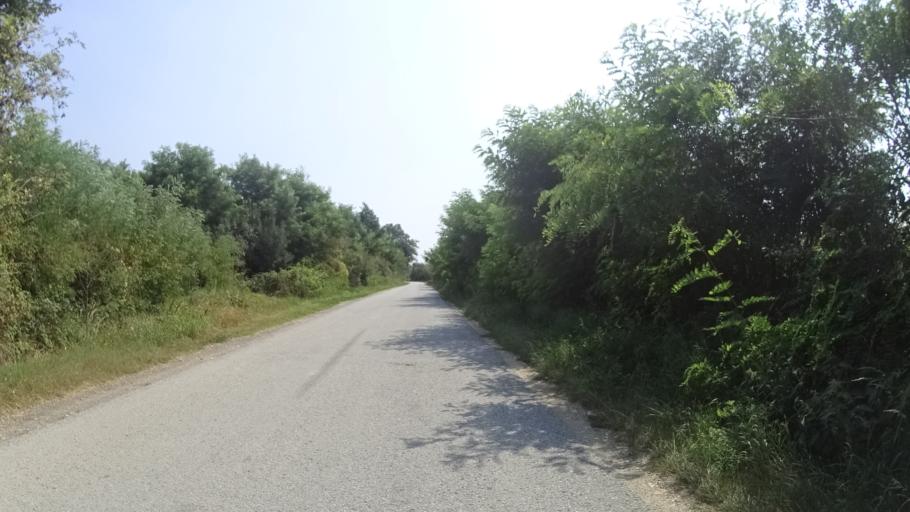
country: HR
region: Medimurska
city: Hodosan
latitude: 46.3945
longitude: 16.6125
